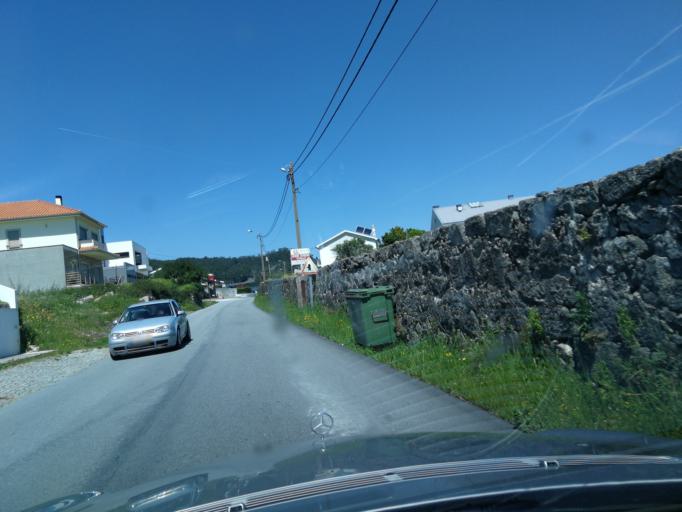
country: PT
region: Viana do Castelo
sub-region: Viana do Castelo
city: Meadela
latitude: 41.7168
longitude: -8.7986
